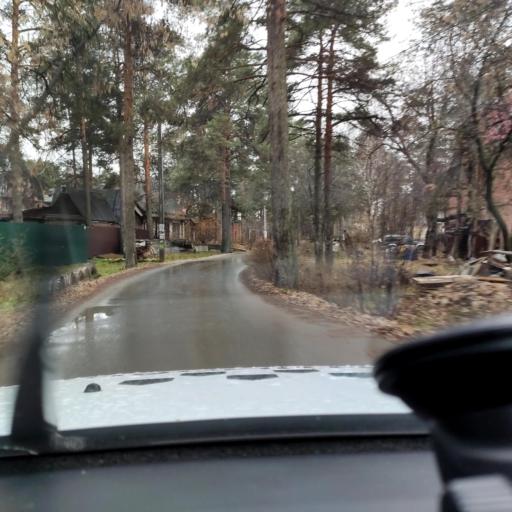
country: RU
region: Perm
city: Perm
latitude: 58.0572
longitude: 56.3015
